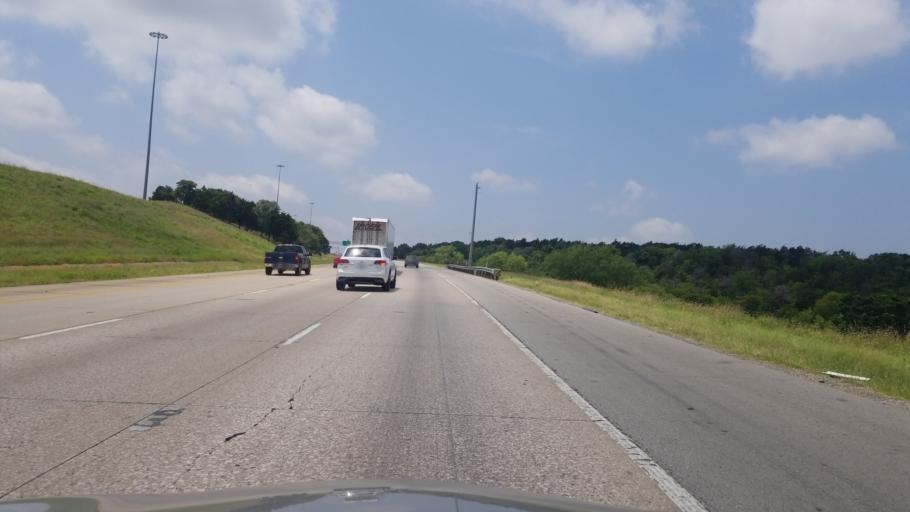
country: US
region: Texas
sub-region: Dallas County
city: Duncanville
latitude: 32.6822
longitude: -96.9452
